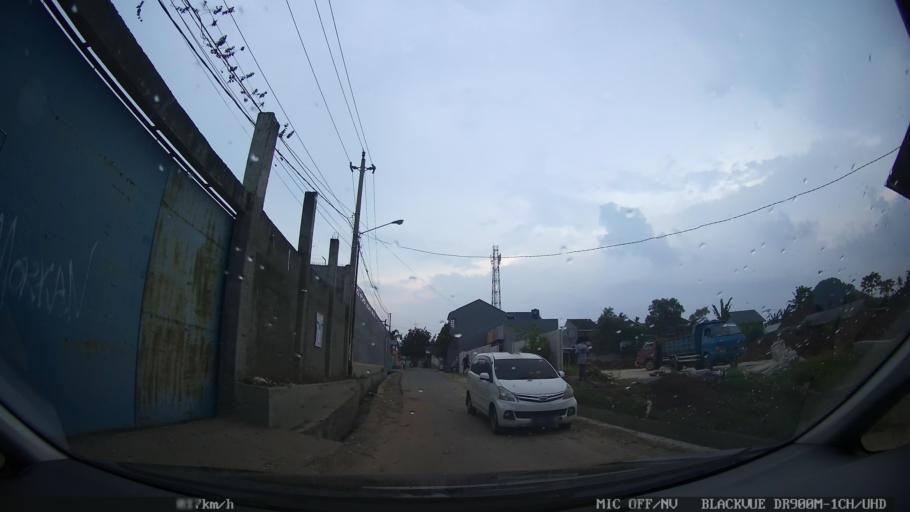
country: ID
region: Lampung
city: Kedaton
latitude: -5.3959
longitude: 105.2754
